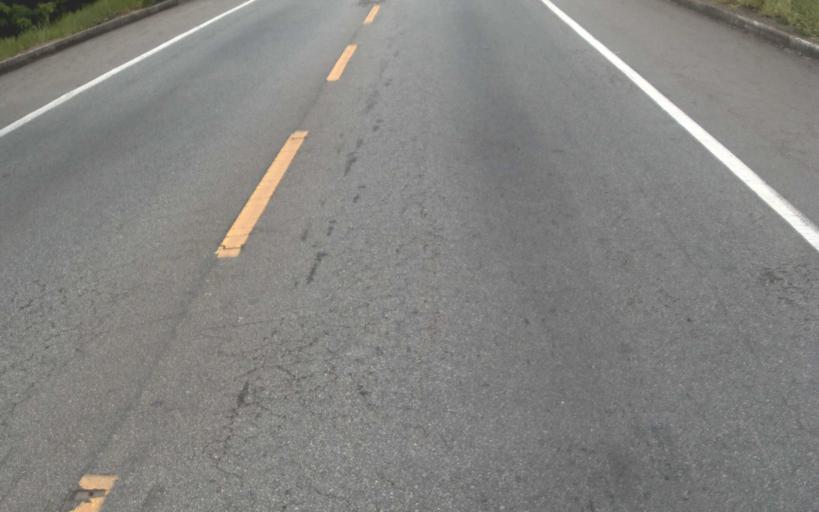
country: BR
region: Minas Gerais
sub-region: Coronel Fabriciano
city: Coronel Fabriciano
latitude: -19.5300
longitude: -42.6128
